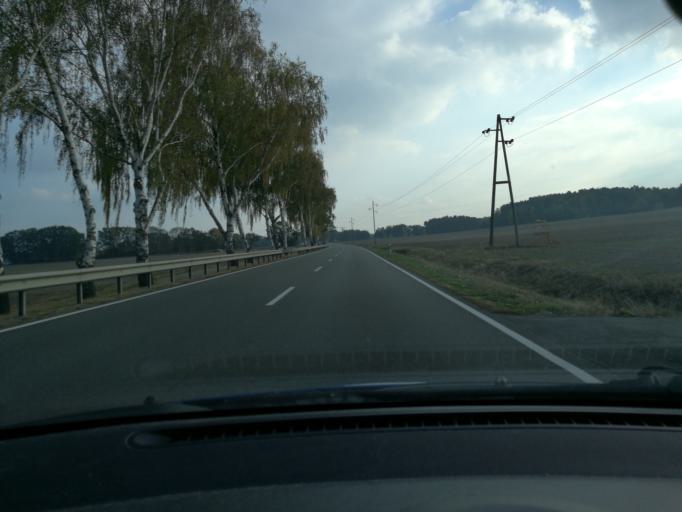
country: DE
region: Lower Saxony
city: Dannenberg
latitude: 53.0967
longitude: 11.0615
